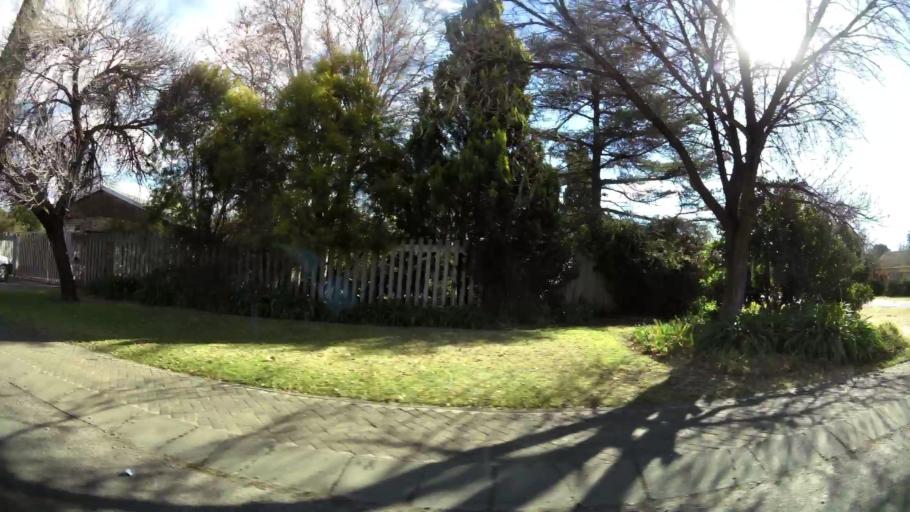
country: ZA
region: North-West
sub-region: Dr Kenneth Kaunda District Municipality
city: Klerksdorp
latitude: -26.8341
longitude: 26.6560
